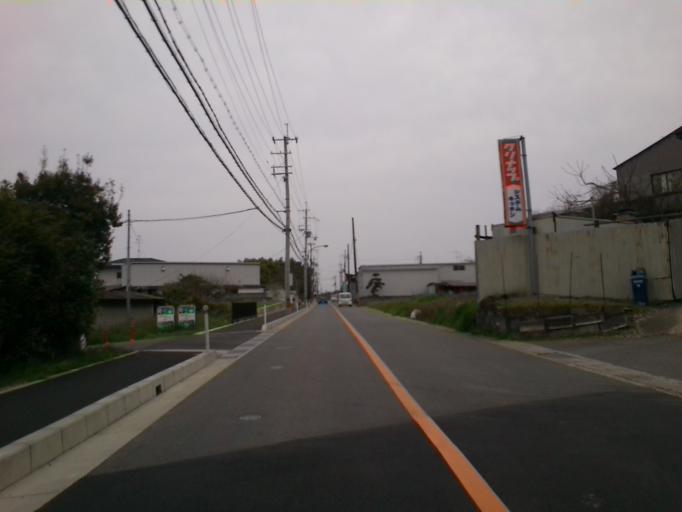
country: JP
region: Kyoto
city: Tanabe
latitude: 34.8426
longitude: 135.7396
